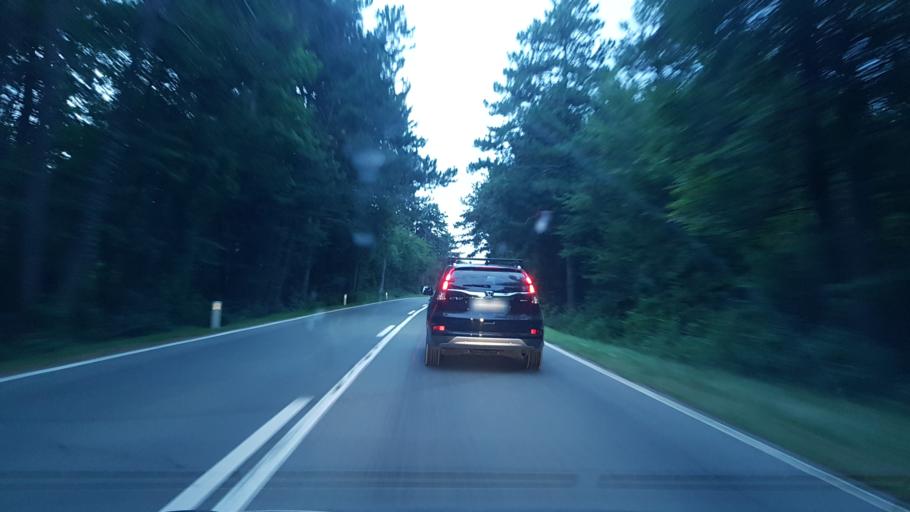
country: SI
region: Divaca
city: Divaca
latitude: 45.6888
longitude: 13.9799
